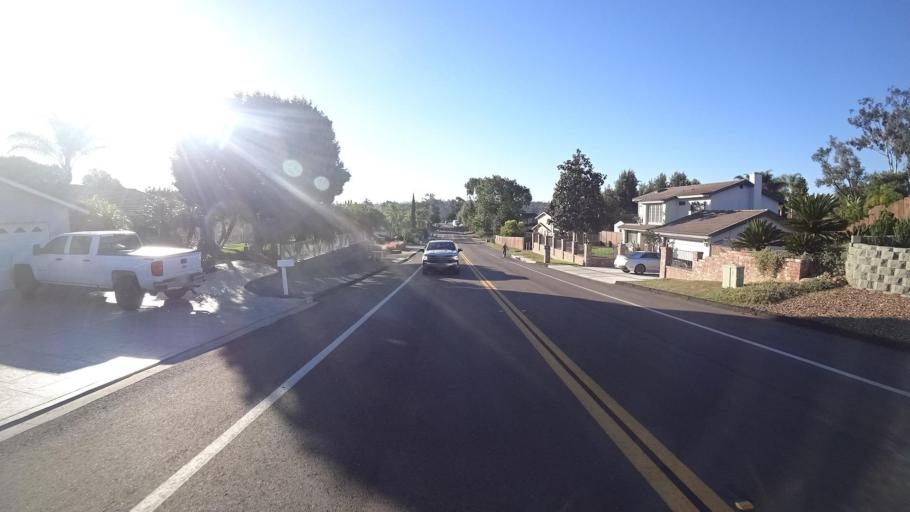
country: US
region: California
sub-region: San Diego County
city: Bonita
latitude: 32.6710
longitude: -117.0309
